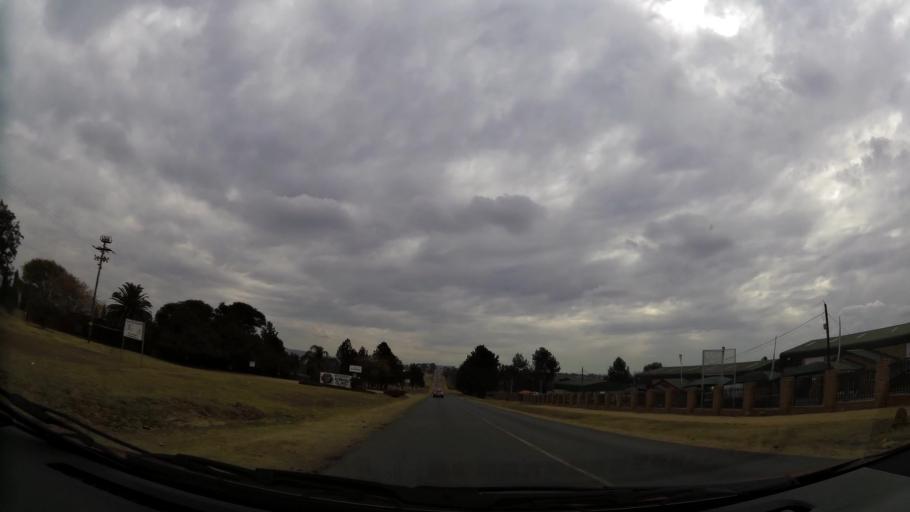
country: ZA
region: Gauteng
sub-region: West Rand District Municipality
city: Muldersdriseloop
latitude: -26.0510
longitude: 27.8927
